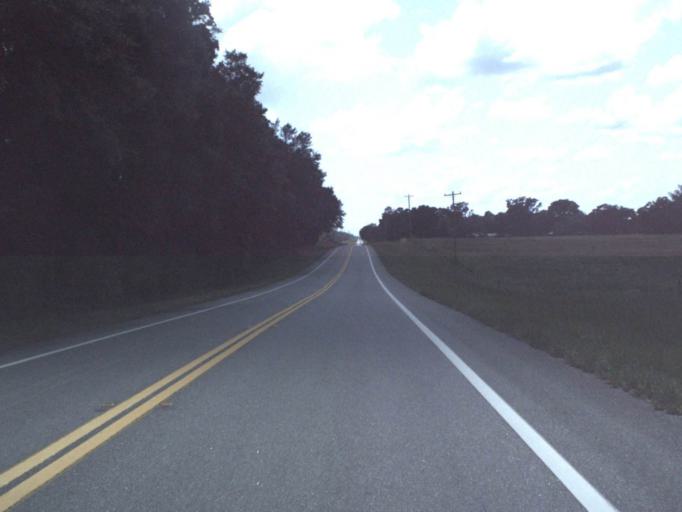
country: US
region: Florida
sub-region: Gilchrist County
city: Trenton
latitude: 29.7310
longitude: -82.7443
